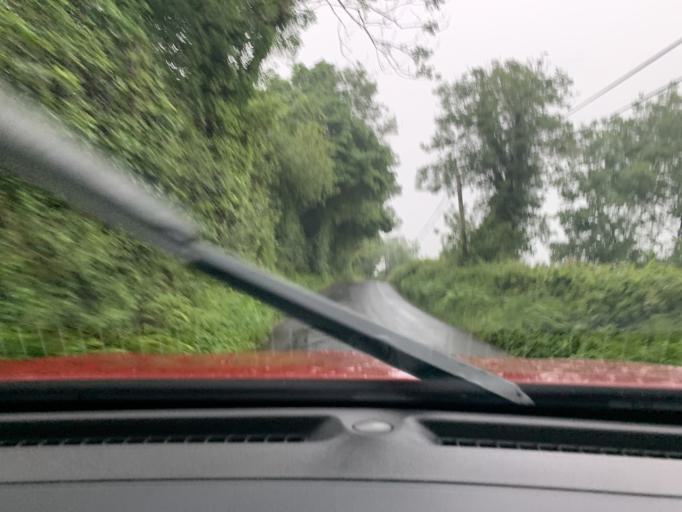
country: IE
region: Connaught
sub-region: Sligo
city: Sligo
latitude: 54.3293
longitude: -8.4190
